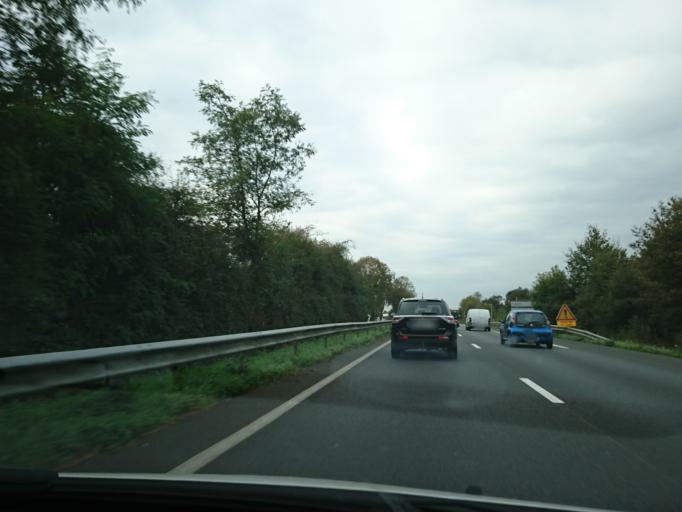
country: FR
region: Pays de la Loire
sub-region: Departement de la Loire-Atlantique
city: Vigneux-de-Bretagne
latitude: 47.2875
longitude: -1.7361
